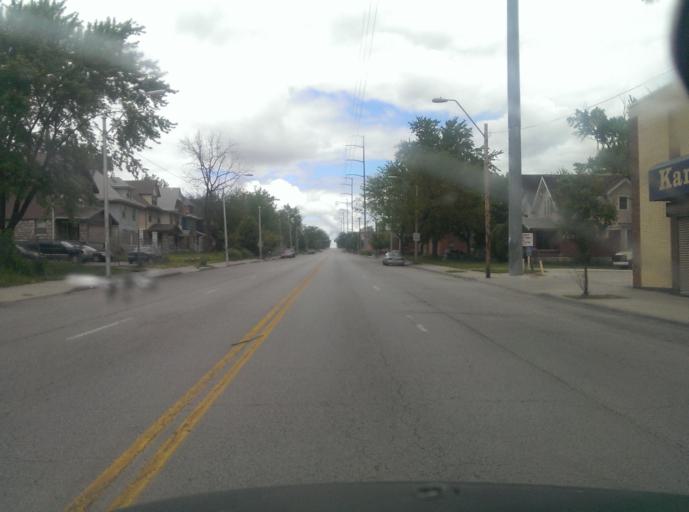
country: US
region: Kansas
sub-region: Johnson County
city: Westwood
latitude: 39.0452
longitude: -94.5727
